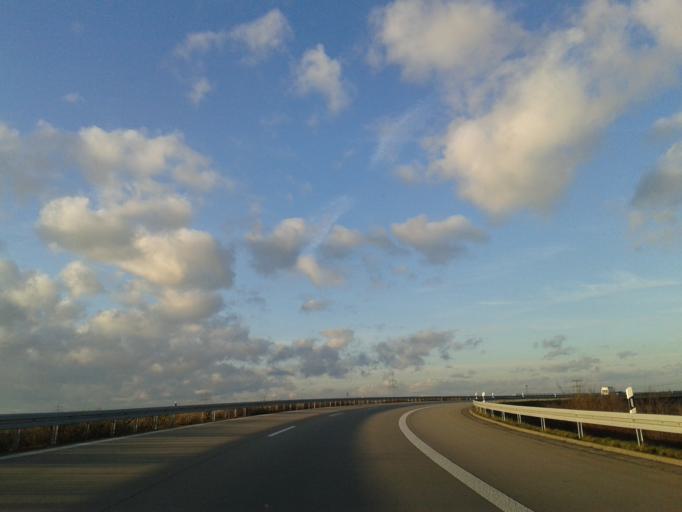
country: DE
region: Saxony-Anhalt
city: Bad Lauchstadt
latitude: 51.4024
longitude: 11.8580
